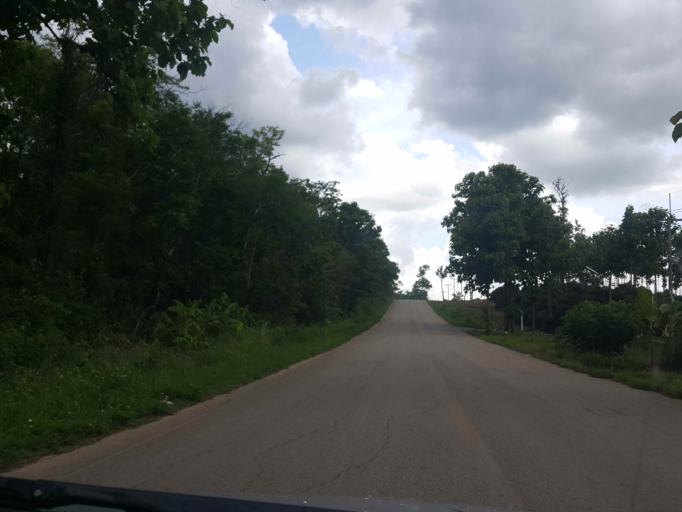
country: TH
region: Phayao
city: Dok Kham Tai
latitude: 18.9755
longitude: 100.0722
